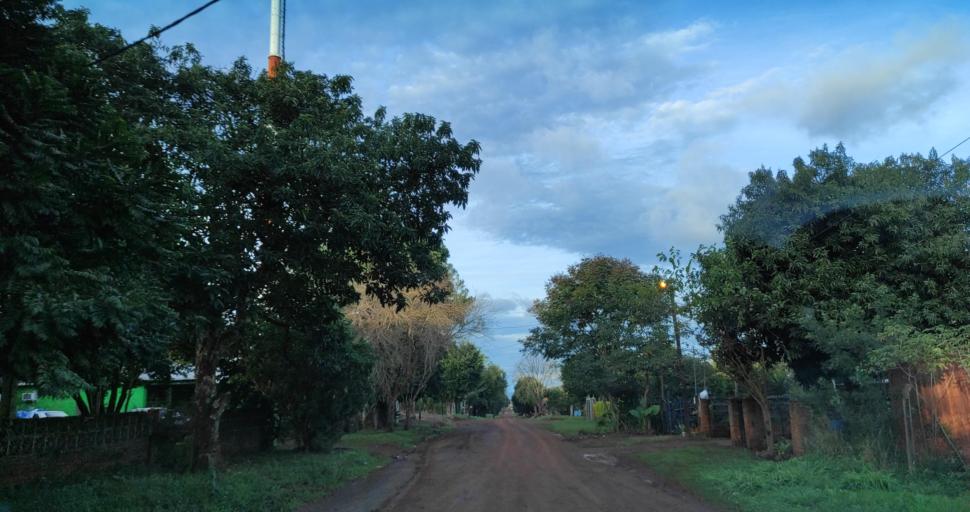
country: AR
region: Misiones
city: Garupa
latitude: -27.4818
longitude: -55.8617
